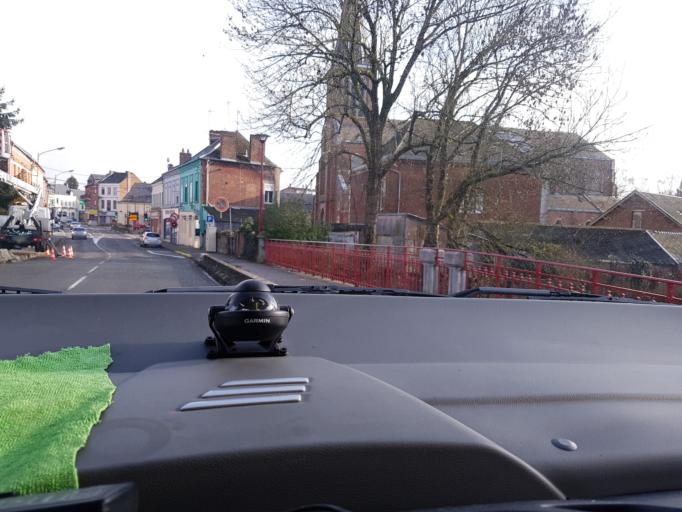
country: FR
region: Picardie
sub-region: Departement de l'Aisne
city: Hirson
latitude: 49.9245
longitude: 4.0784
